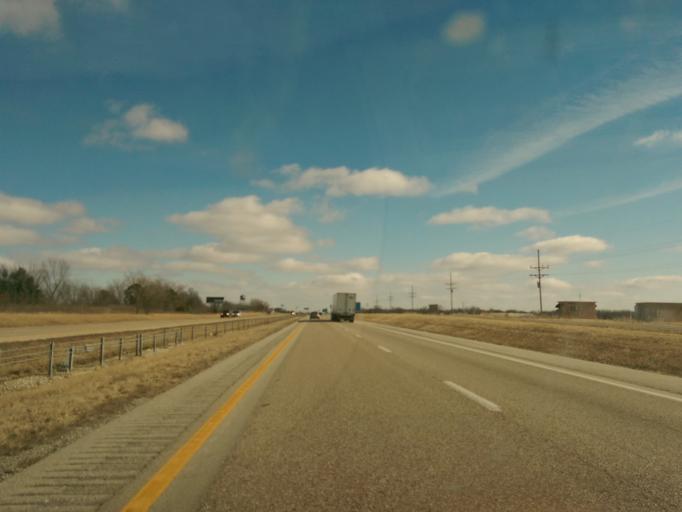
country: US
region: Missouri
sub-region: Montgomery County
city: Montgomery City
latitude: 38.9035
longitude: -91.4841
